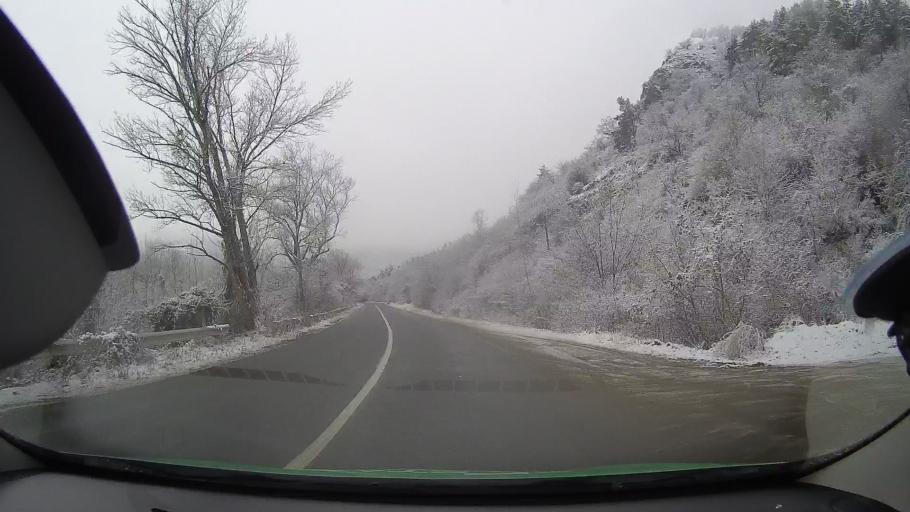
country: RO
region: Cluj
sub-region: Comuna Moldovenesti
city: Moldovenesti
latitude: 46.5114
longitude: 23.6608
